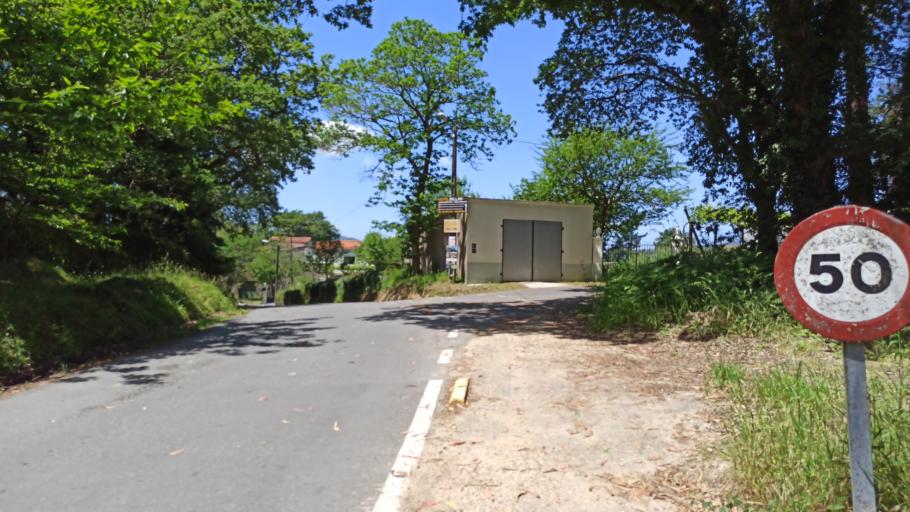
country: ES
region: Galicia
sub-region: Provincia da Coruna
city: Negreira
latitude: 42.9085
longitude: -8.7259
